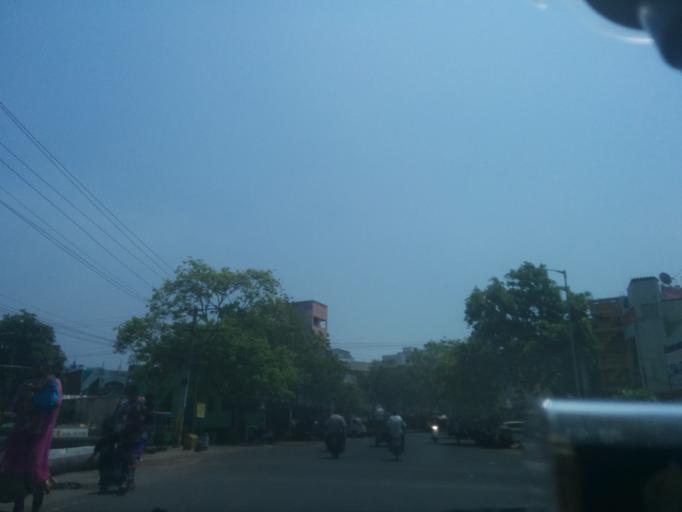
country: IN
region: Andhra Pradesh
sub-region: East Godavari
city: Rajahmundry
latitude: 17.0173
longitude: 81.7727
